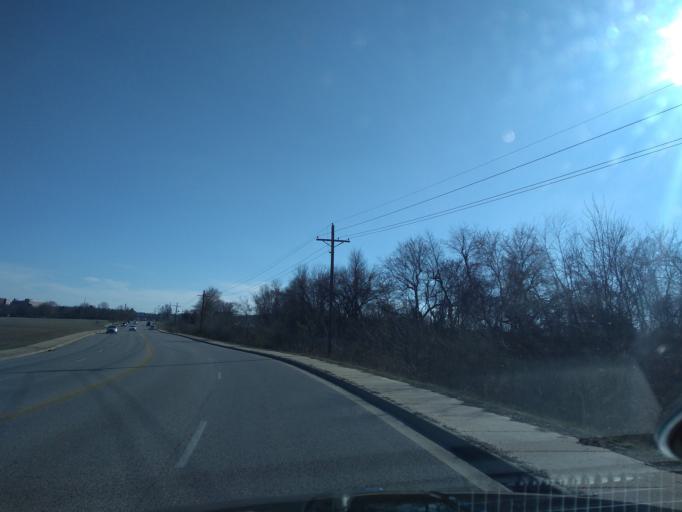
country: US
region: Arkansas
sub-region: Washington County
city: Johnson
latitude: 36.1218
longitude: -94.1634
